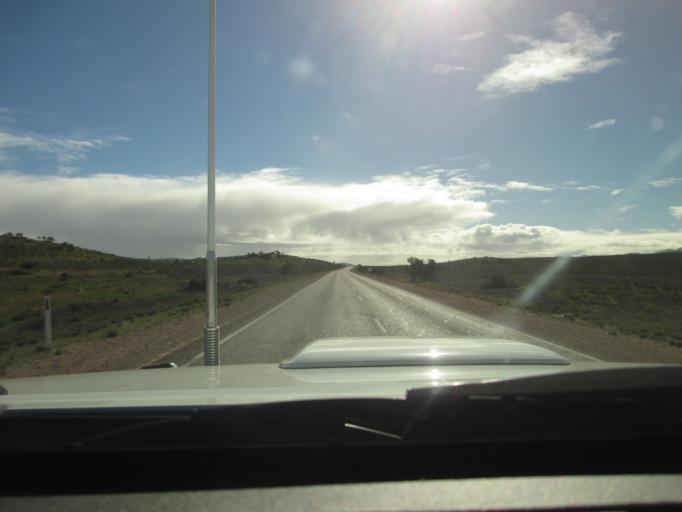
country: AU
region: South Australia
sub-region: Flinders Ranges
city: Quorn
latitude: -31.7461
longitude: 138.3373
